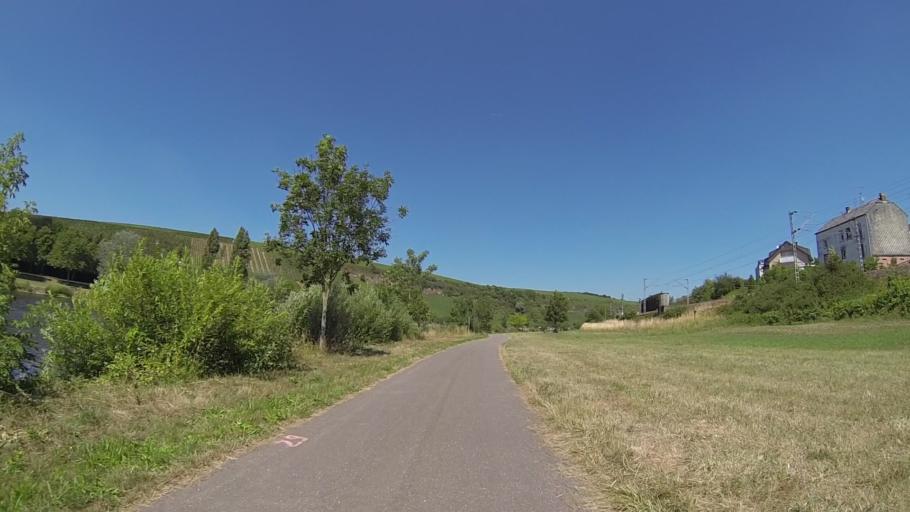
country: LU
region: Grevenmacher
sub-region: Canton de Remich
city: Lenningen
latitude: 49.5873
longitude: 6.3756
